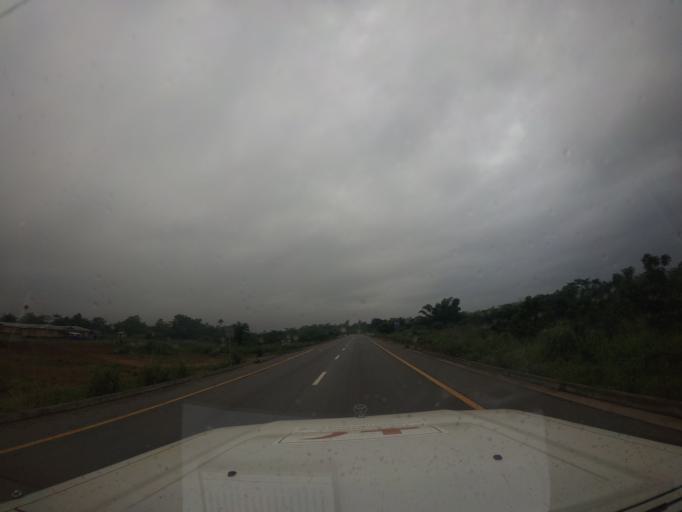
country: SL
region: Eastern Province
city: Hangha
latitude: 7.9444
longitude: -11.1387
